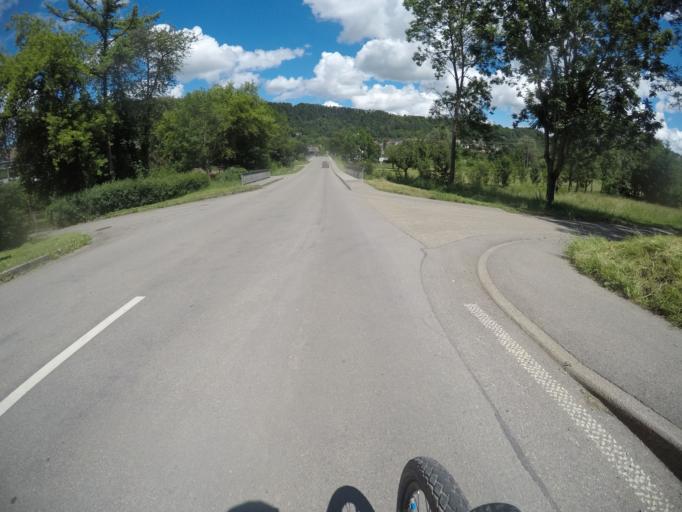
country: DE
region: Baden-Wuerttemberg
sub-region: Tuebingen Region
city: Haigerloch
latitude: 48.4429
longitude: 8.8001
